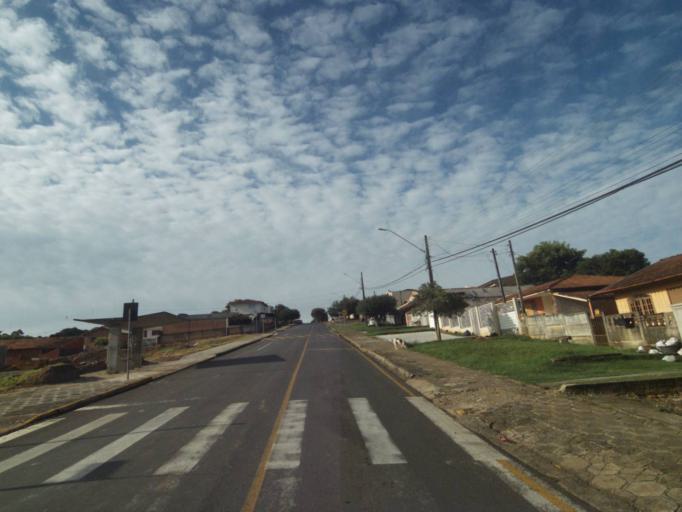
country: BR
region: Parana
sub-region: Telemaco Borba
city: Telemaco Borba
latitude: -24.3447
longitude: -50.6122
